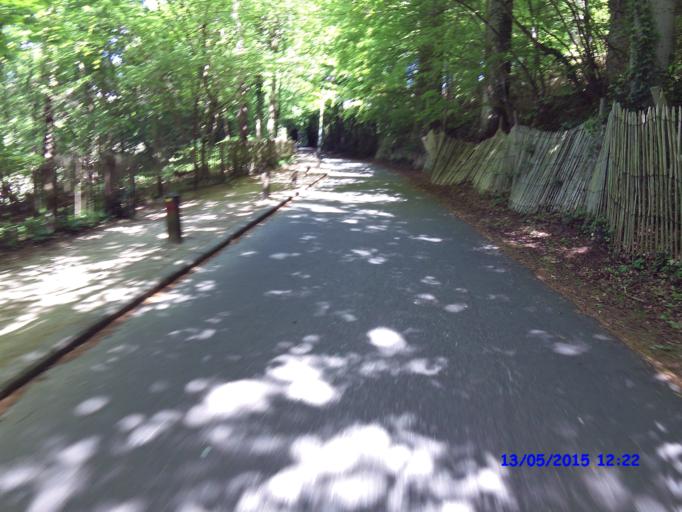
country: BE
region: Flanders
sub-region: Provincie Vlaams-Brabant
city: Kraainem
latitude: 50.8152
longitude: 4.4413
